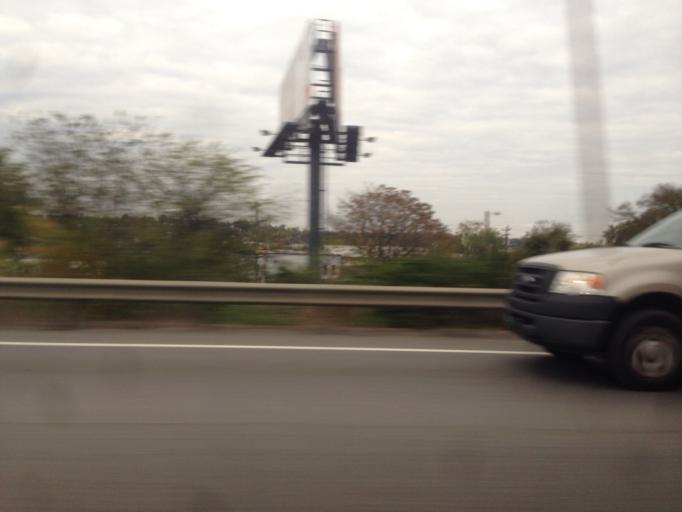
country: US
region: Tennessee
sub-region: Davidson County
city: Nashville
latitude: 36.1530
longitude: -86.7554
